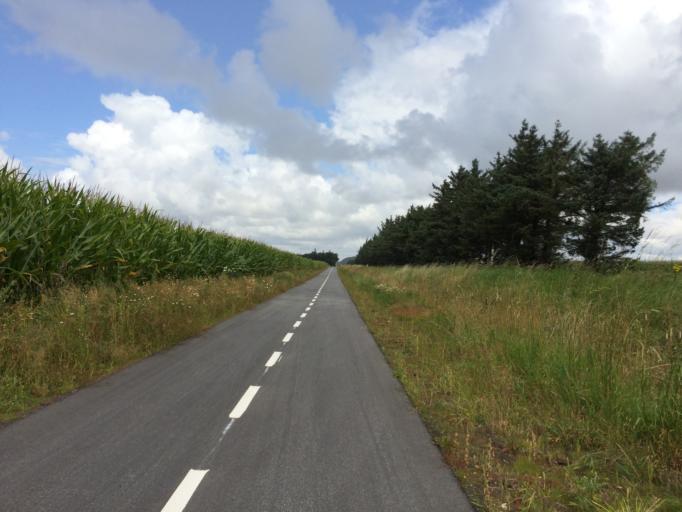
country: DK
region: Central Jutland
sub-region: Holstebro Kommune
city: Ulfborg
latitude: 56.3032
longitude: 8.3386
